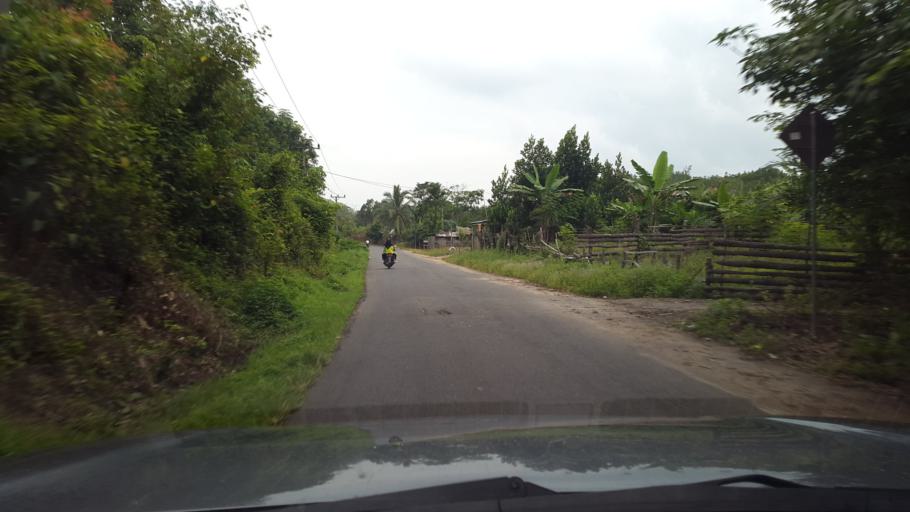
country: ID
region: South Sumatra
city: Gunungmenang
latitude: -3.1688
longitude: 104.0017
